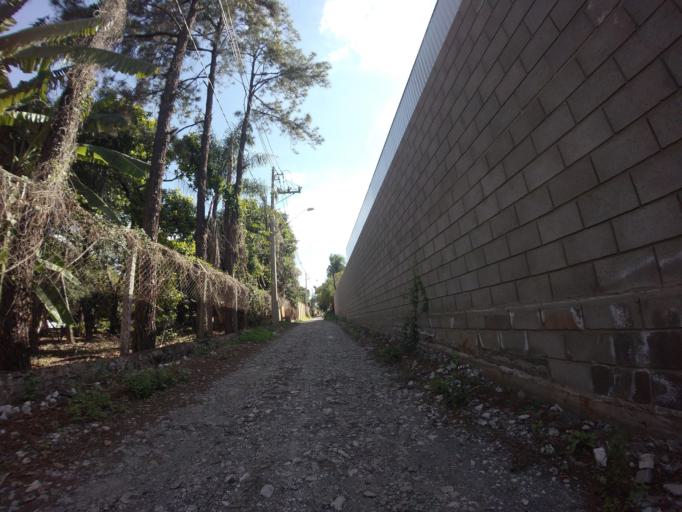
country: BR
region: Sao Paulo
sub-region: Piracicaba
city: Piracicaba
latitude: -22.7322
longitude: -47.5958
